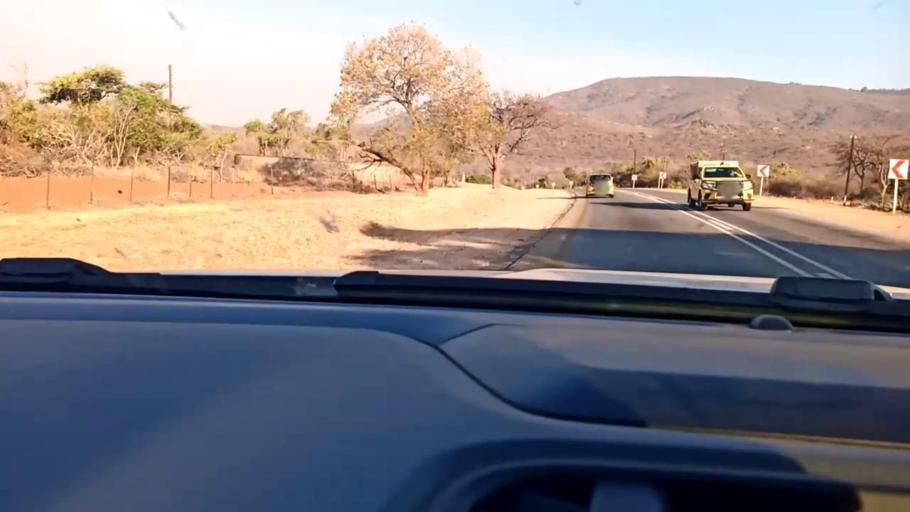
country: ZA
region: Limpopo
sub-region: Mopani District Municipality
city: Duiwelskloof
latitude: -23.6276
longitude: 30.1308
